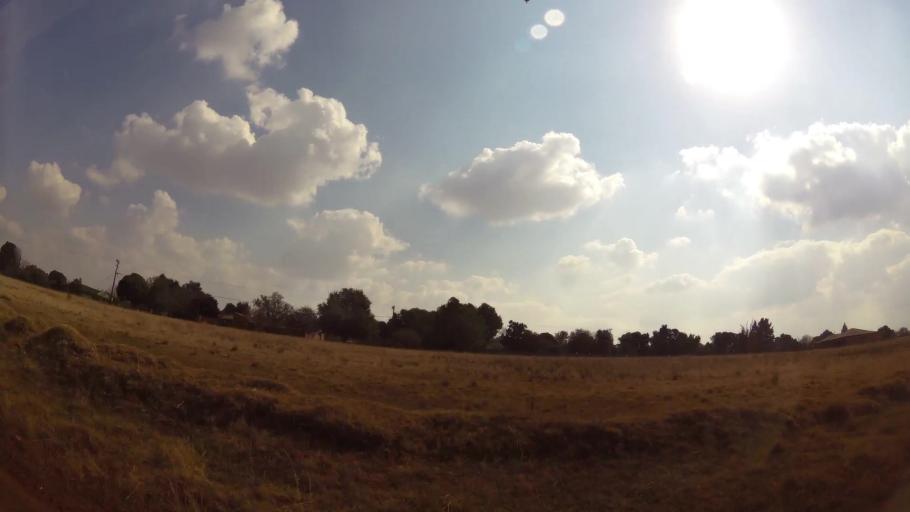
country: ZA
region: Mpumalanga
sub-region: Nkangala District Municipality
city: Delmas
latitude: -26.1554
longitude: 28.5575
